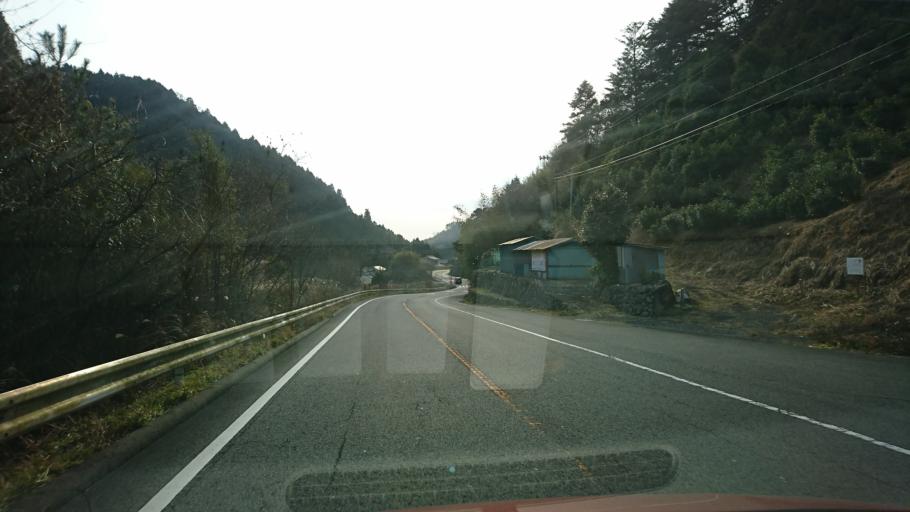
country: JP
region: Ehime
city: Hojo
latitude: 33.9272
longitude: 132.8928
